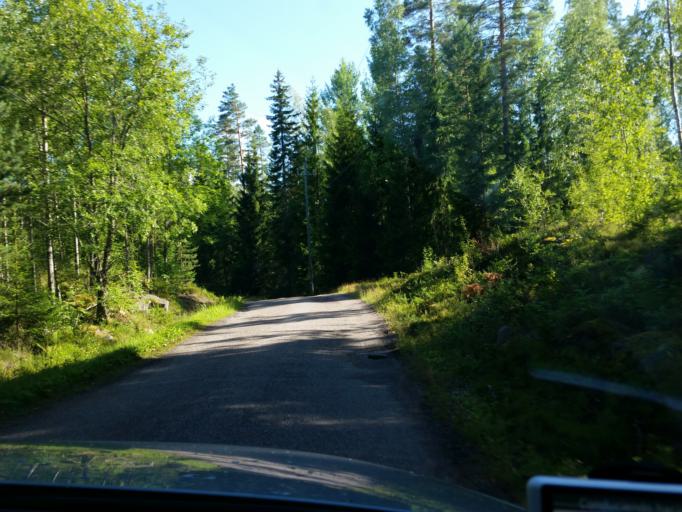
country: FI
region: Uusimaa
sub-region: Helsinki
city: Kaerkoelae
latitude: 60.5612
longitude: 24.0027
